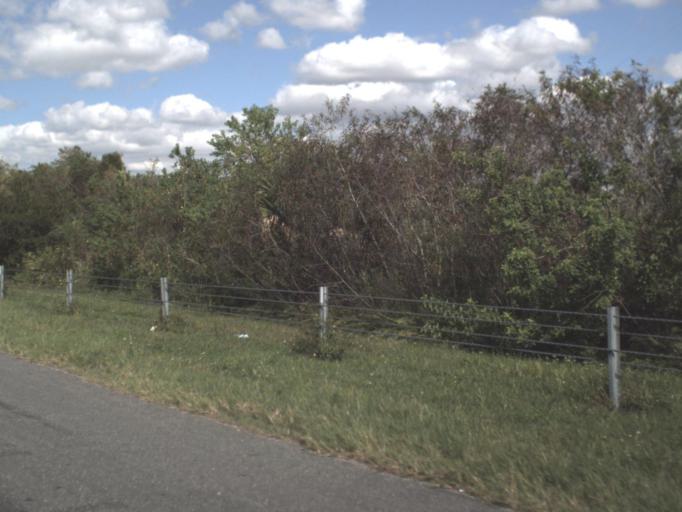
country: US
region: Florida
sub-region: Osceola County
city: Buenaventura Lakes
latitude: 28.2930
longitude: -81.3521
